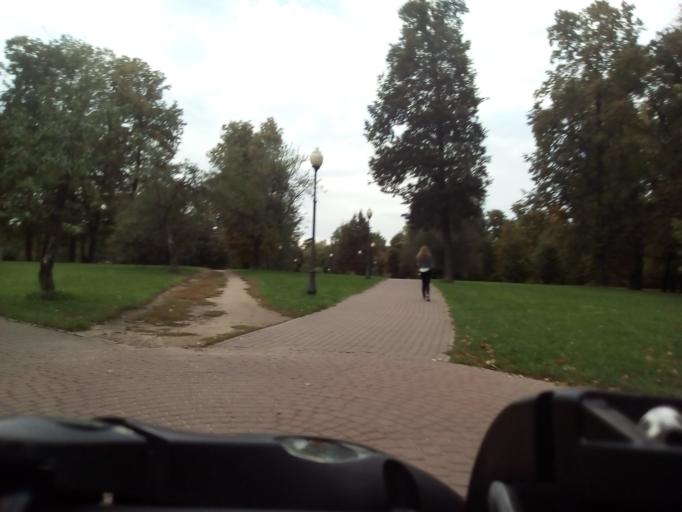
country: RU
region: Moscow
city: Sviblovo
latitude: 55.8414
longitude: 37.6411
